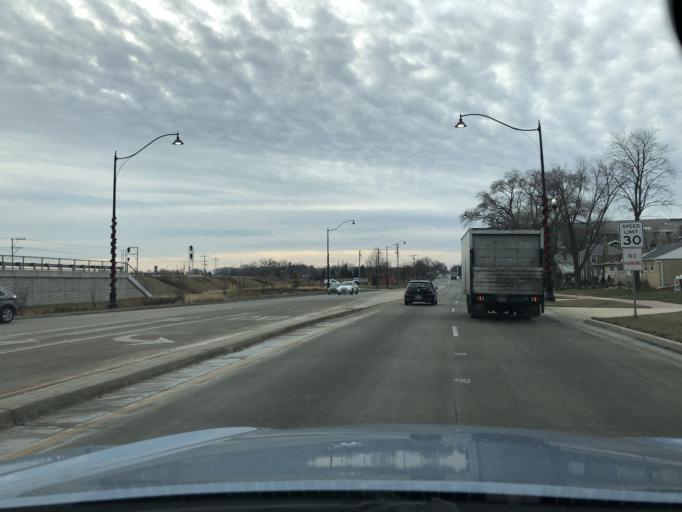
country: US
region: Illinois
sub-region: DuPage County
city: Bensenville
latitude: 41.9603
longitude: -87.9397
